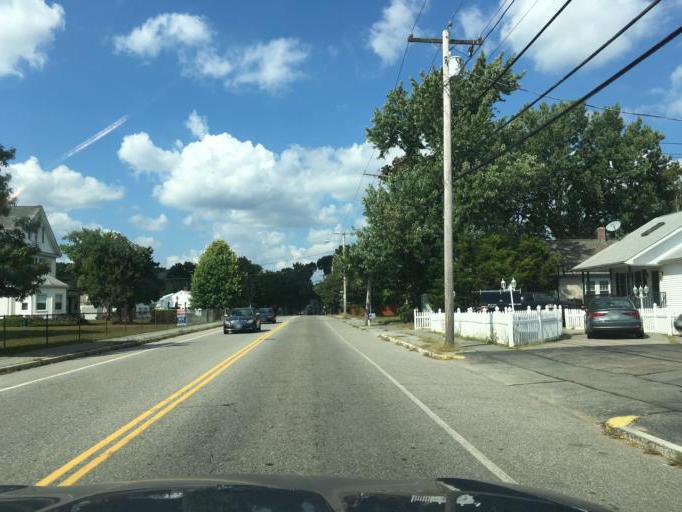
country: US
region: Rhode Island
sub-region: Kent County
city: Warwick
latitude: 41.6925
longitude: -71.3983
